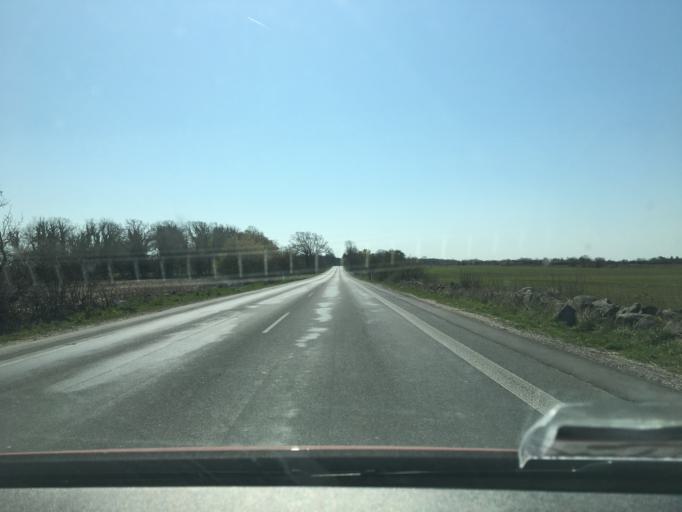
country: DK
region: Zealand
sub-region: Guldborgsund Kommune
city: Nykobing Falster
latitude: 54.7312
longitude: 11.7977
